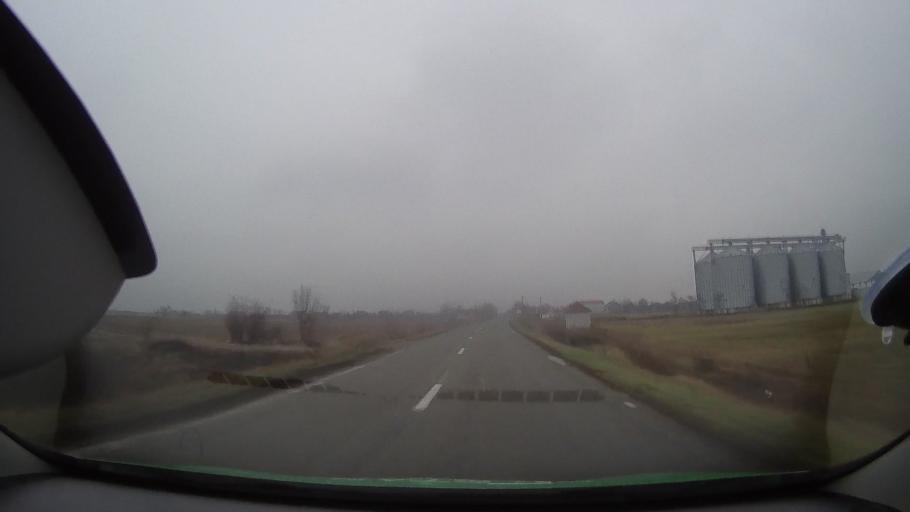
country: RO
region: Bihor
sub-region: Comuna Tulca
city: Tulca
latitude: 46.7947
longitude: 21.7383
